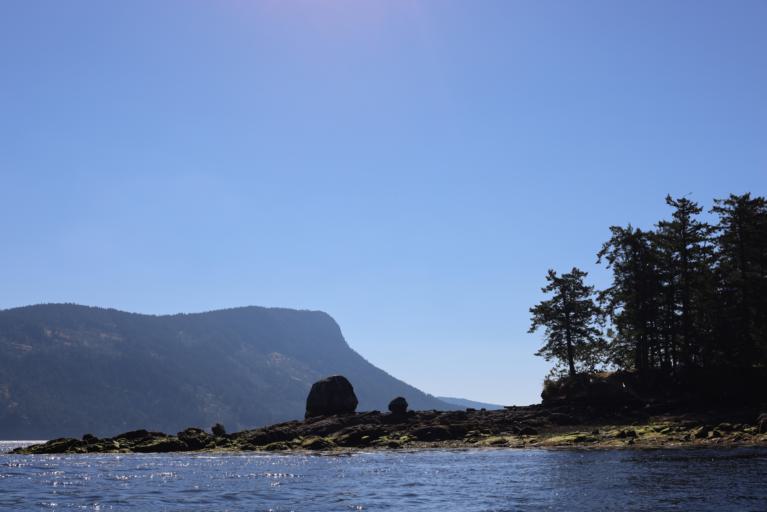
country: CA
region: British Columbia
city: North Cowichan
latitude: 48.8087
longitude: -123.5901
